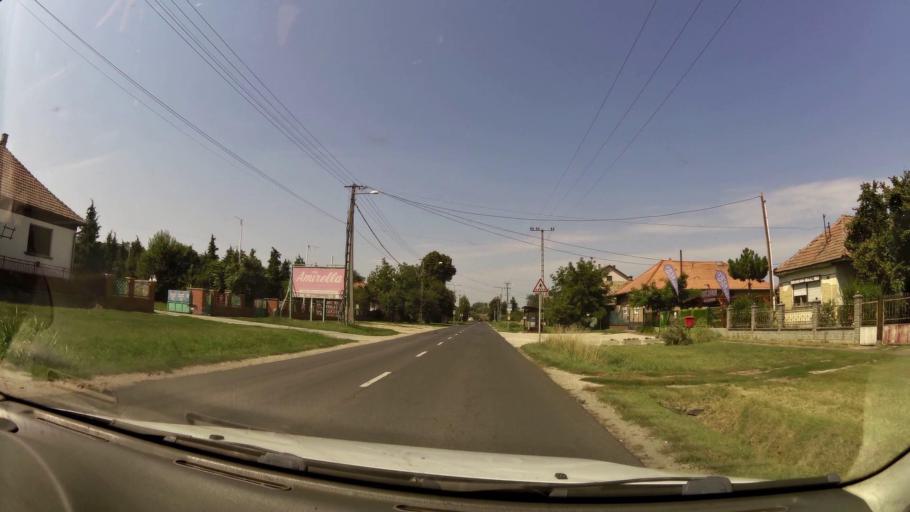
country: HU
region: Pest
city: Suelysap
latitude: 47.4460
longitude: 19.5457
